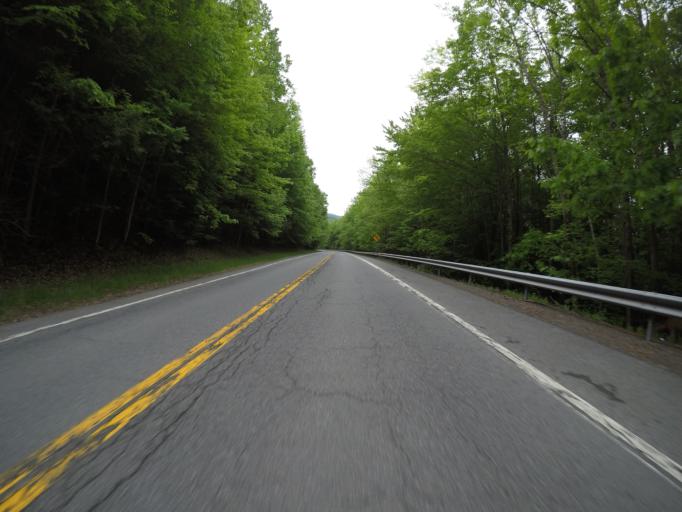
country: US
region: New York
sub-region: Sullivan County
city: Livingston Manor
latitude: 42.0808
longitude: -74.8851
